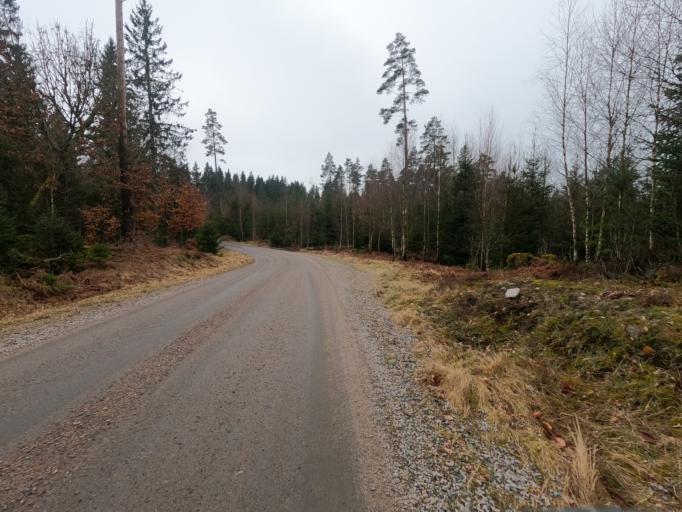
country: SE
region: Kronoberg
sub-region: Markaryds Kommun
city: Stromsnasbruk
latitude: 56.8282
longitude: 13.5634
